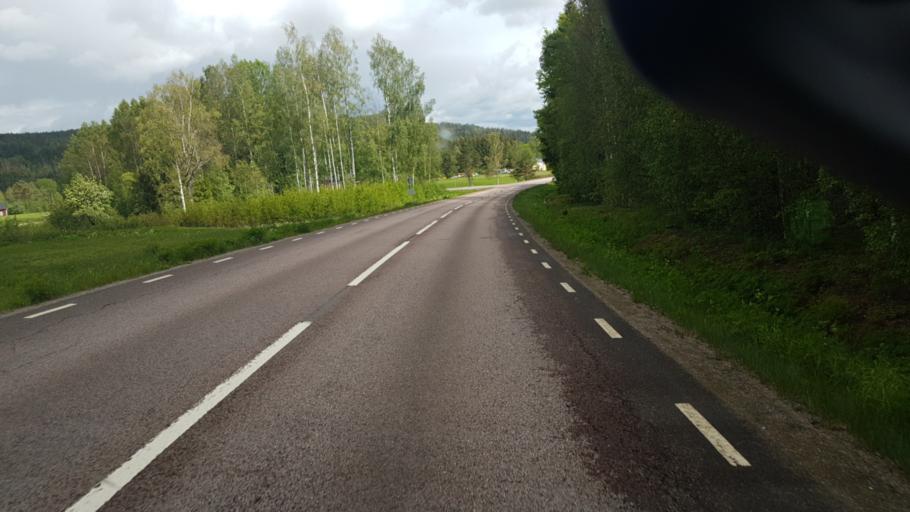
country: SE
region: Vaermland
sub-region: Eda Kommun
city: Amotfors
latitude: 59.6778
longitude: 12.3881
